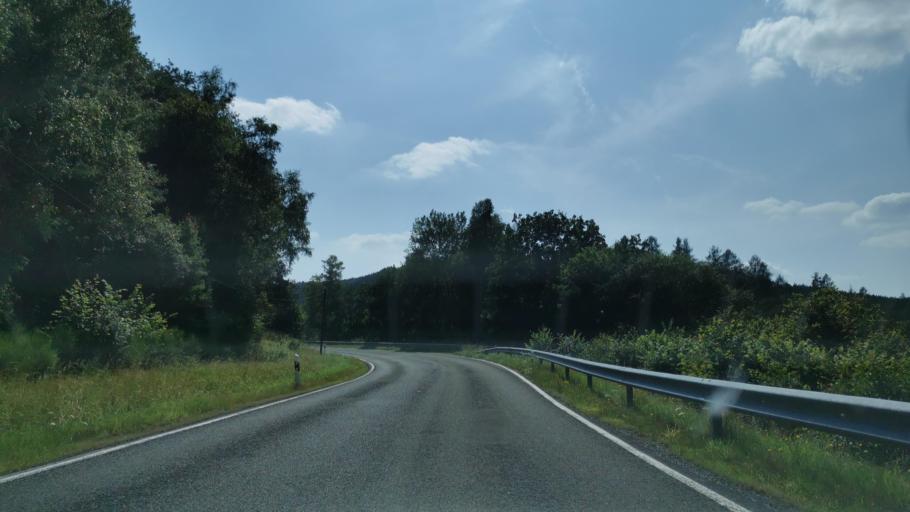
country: DE
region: Rheinland-Pfalz
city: Rorodt
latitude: 49.7801
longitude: 7.0500
